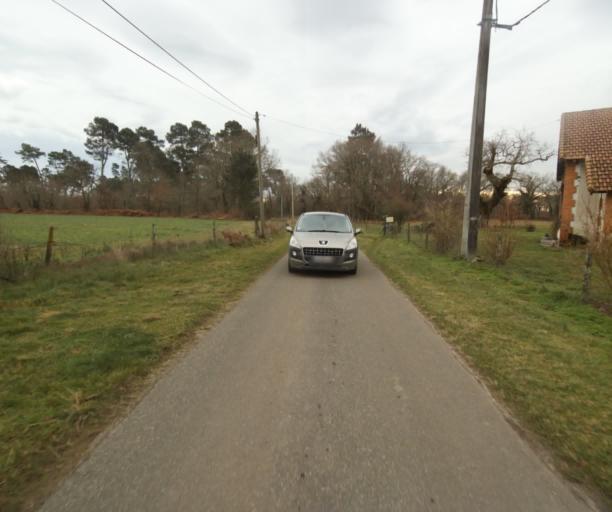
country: FR
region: Aquitaine
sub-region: Departement des Landes
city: Gabarret
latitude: 44.0191
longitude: -0.0633
